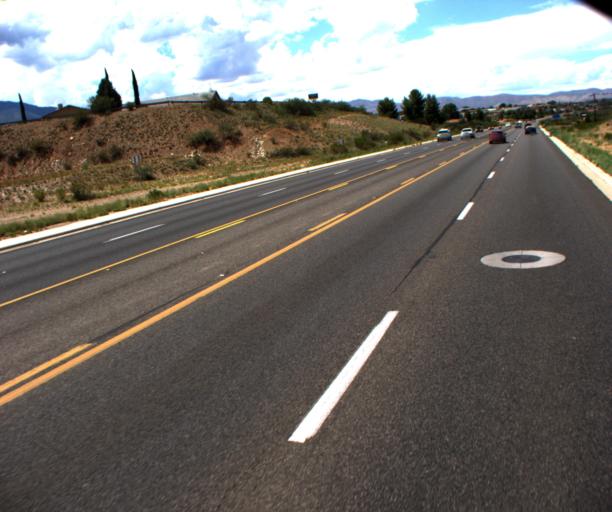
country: US
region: Arizona
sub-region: Yavapai County
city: Verde Village
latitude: 34.7080
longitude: -111.9937
